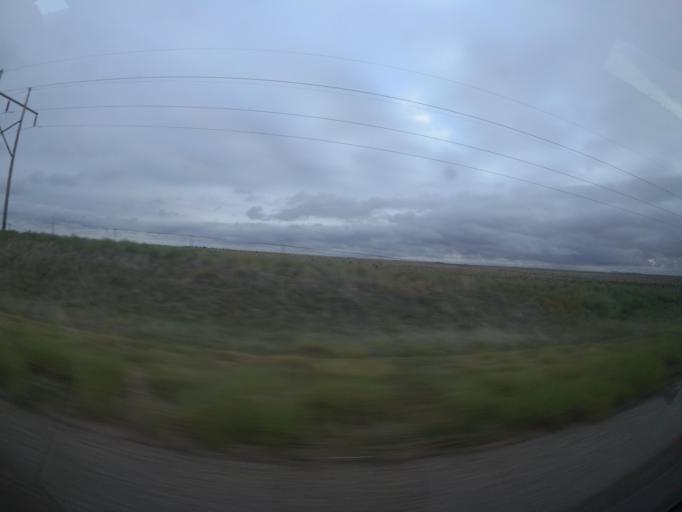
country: US
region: Colorado
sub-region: Yuma County
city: Yuma
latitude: 39.6558
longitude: -102.7303
